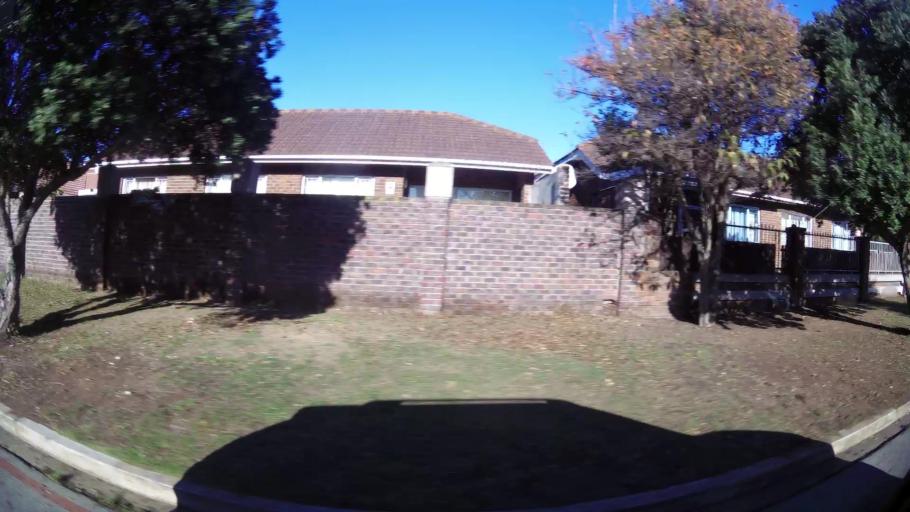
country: ZA
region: Eastern Cape
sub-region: Nelson Mandela Bay Metropolitan Municipality
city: Port Elizabeth
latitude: -33.9895
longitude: 25.6690
